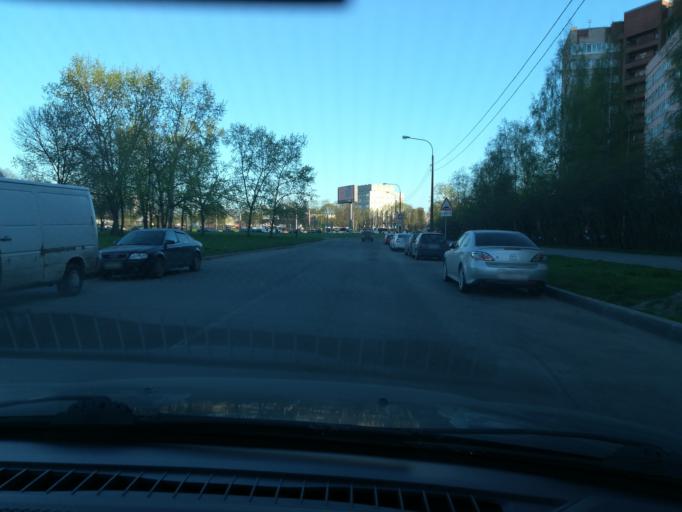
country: RU
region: St.-Petersburg
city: Avtovo
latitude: 59.8622
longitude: 30.2550
